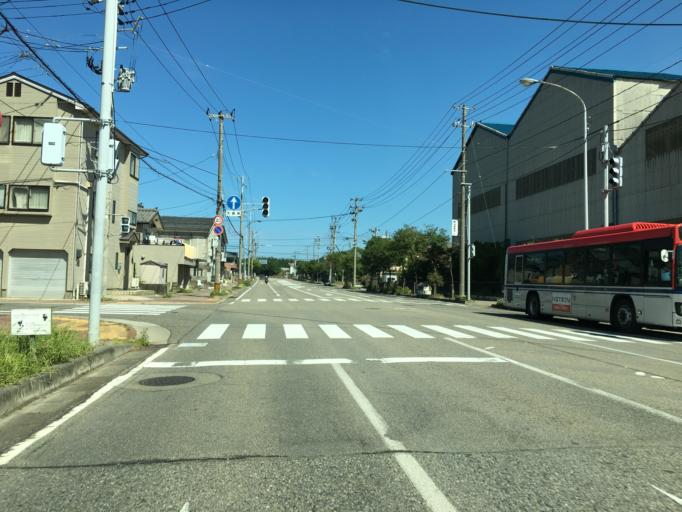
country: JP
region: Niigata
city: Niigata-shi
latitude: 37.9391
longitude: 139.0576
